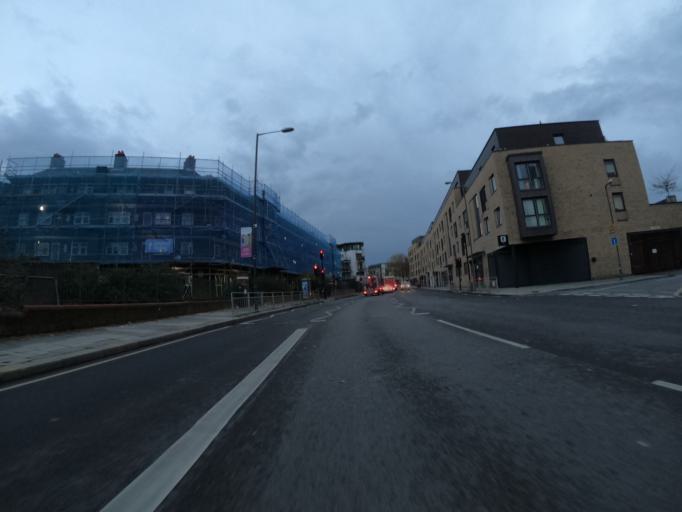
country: GB
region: England
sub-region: Greater London
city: Blackheath
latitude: 51.4872
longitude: 0.0075
